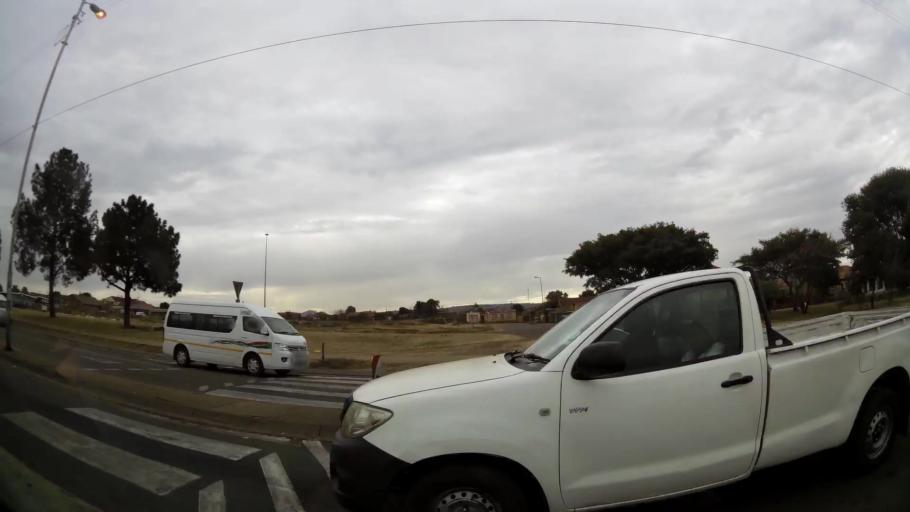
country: ZA
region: Gauteng
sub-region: City of Tshwane Metropolitan Municipality
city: Pretoria
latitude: -25.7184
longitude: 28.3516
